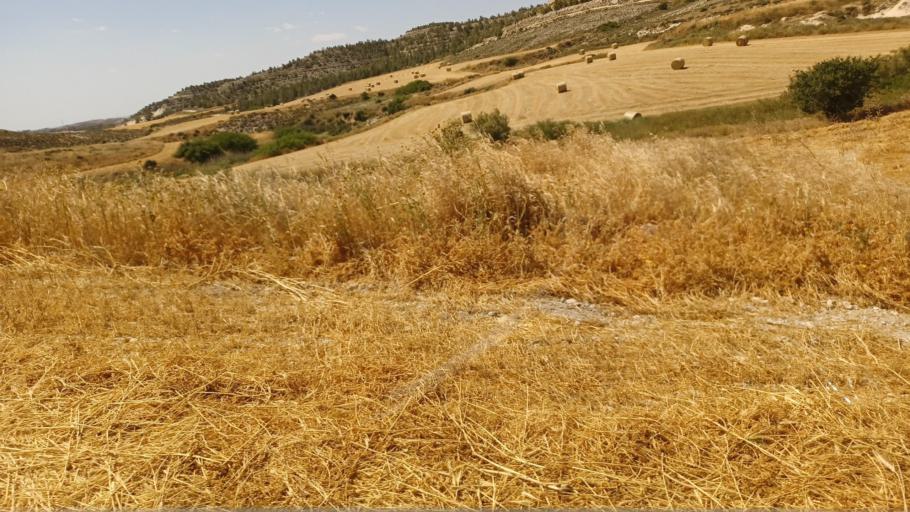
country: CY
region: Lefkosia
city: Lympia
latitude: 34.9910
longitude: 33.5311
